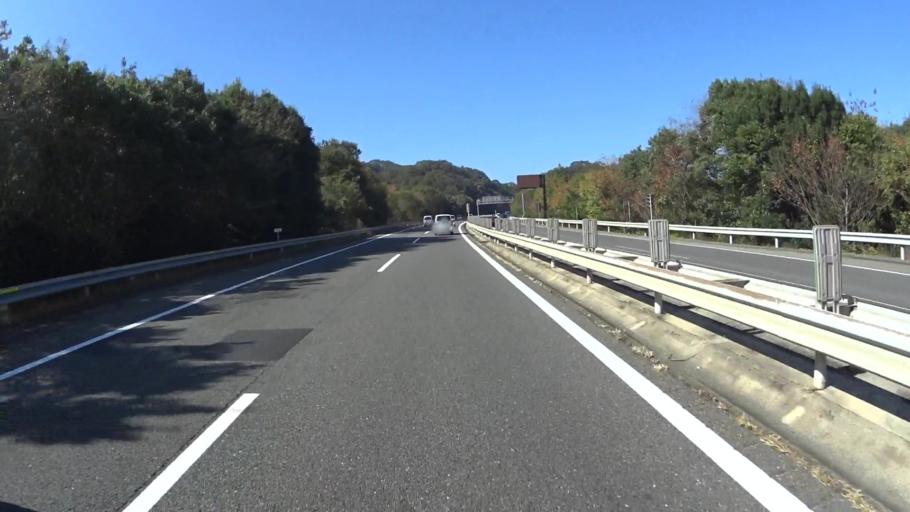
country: JP
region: Kyoto
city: Kameoka
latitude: 34.9897
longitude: 135.6038
